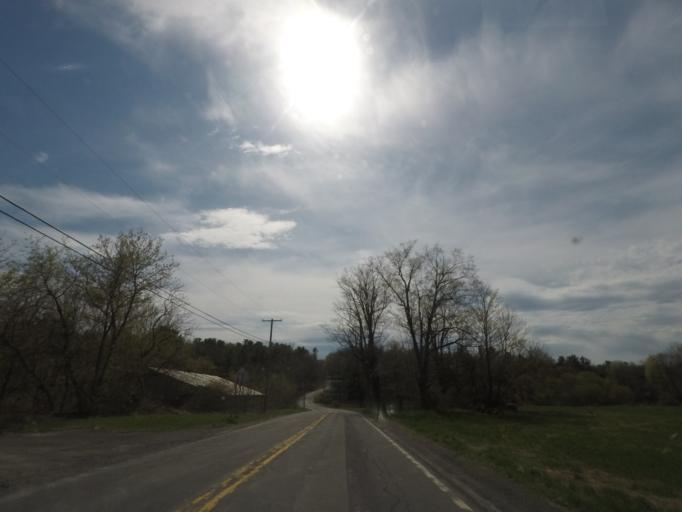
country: US
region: New York
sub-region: Columbia County
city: Chatham
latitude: 42.3484
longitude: -73.5729
